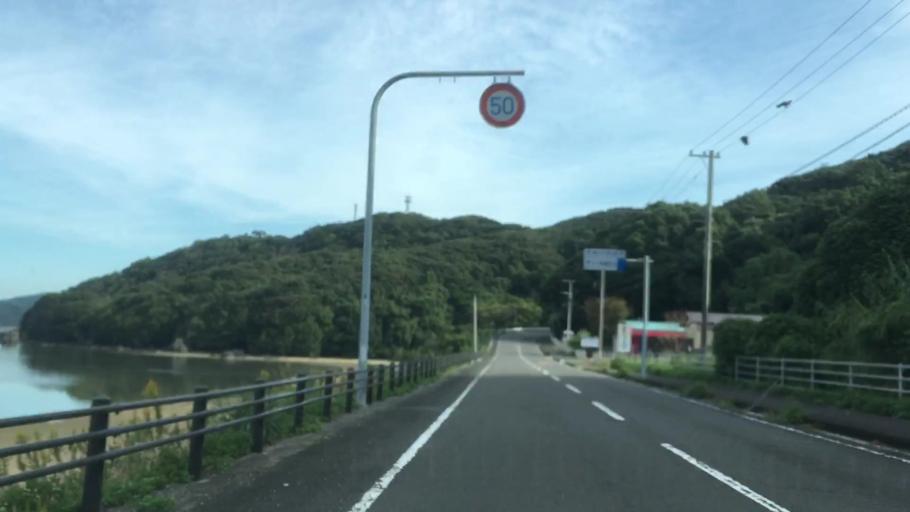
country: JP
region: Nagasaki
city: Sasebo
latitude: 32.9886
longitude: 129.6464
